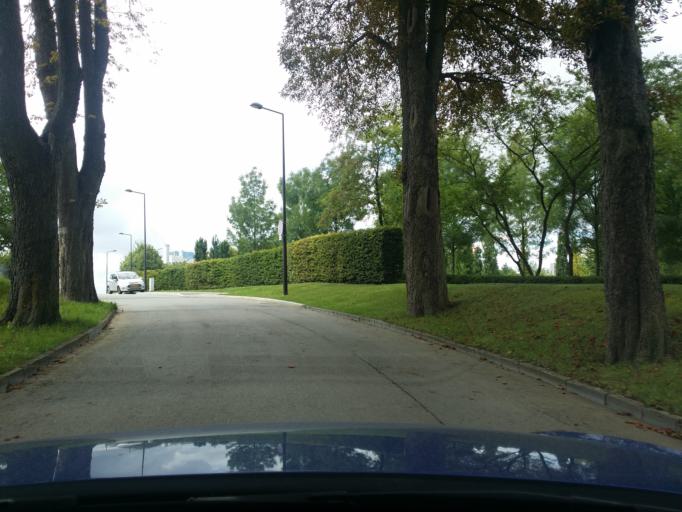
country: LU
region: Luxembourg
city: Kirchberg
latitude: 49.6142
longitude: 6.1752
